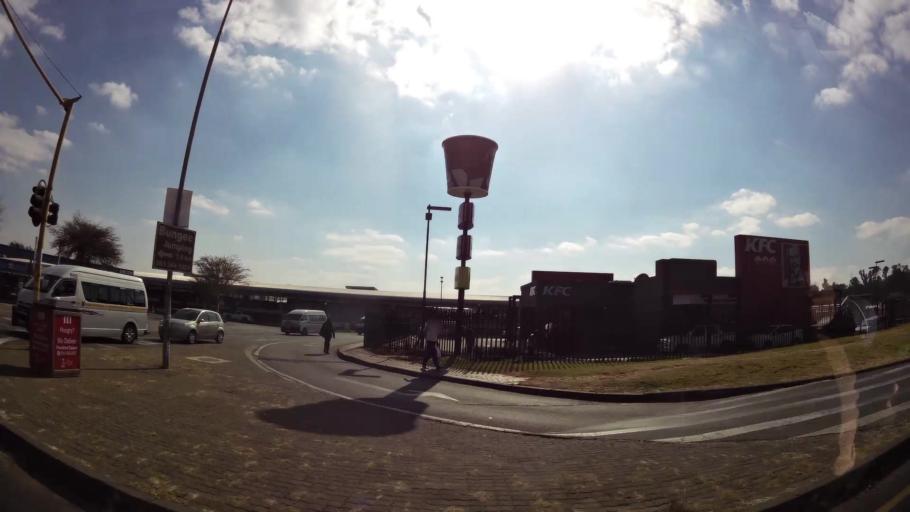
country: ZA
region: Gauteng
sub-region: West Rand District Municipality
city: Krugersdorp
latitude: -26.0889
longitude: 27.7829
